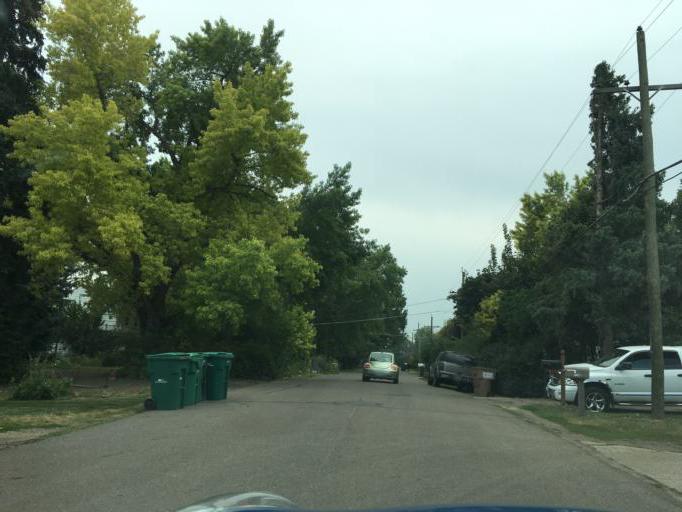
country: US
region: Colorado
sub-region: Jefferson County
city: Wheat Ridge
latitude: 39.7441
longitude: -105.1014
